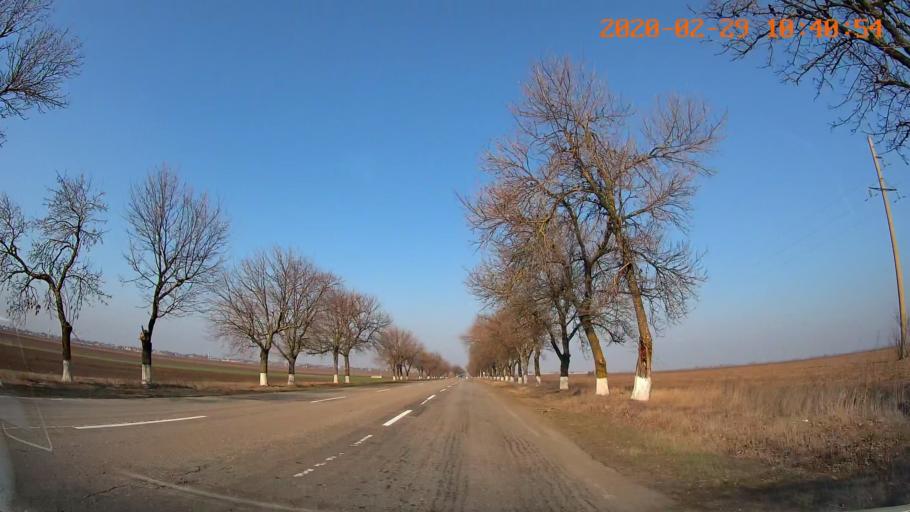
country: MD
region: Anenii Noi
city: Varnita
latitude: 47.0374
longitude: 29.4329
